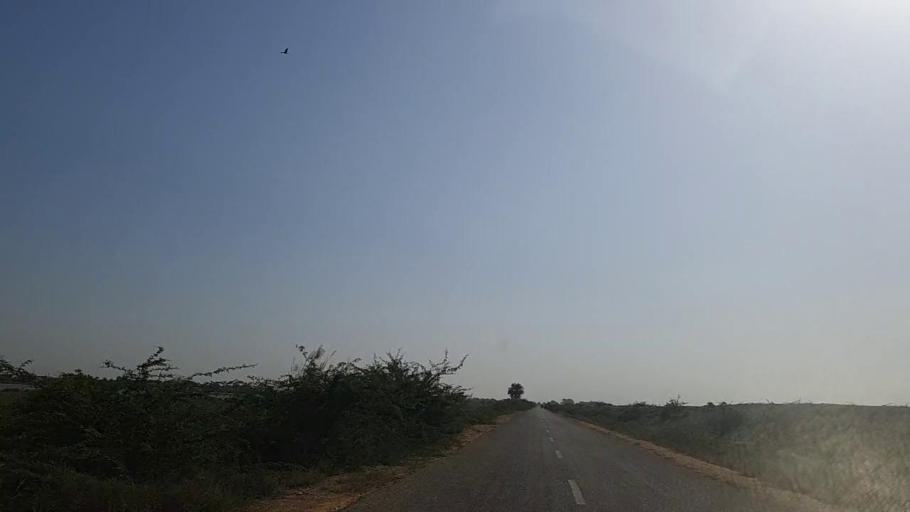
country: PK
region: Sindh
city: Jati
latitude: 24.4379
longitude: 68.2607
